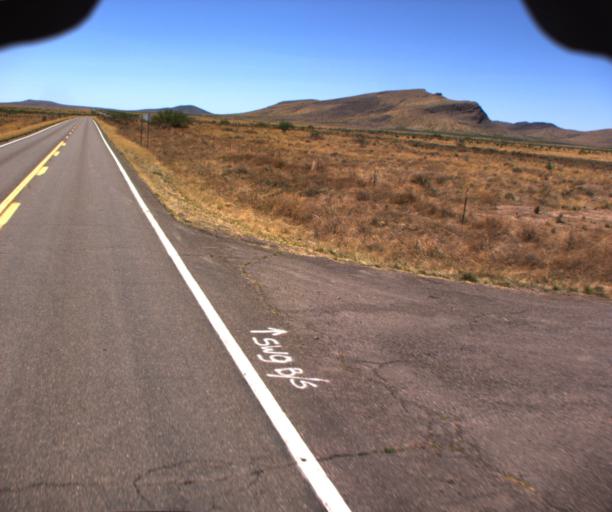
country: US
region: Arizona
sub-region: Cochise County
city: Douglas
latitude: 31.6898
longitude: -109.1330
